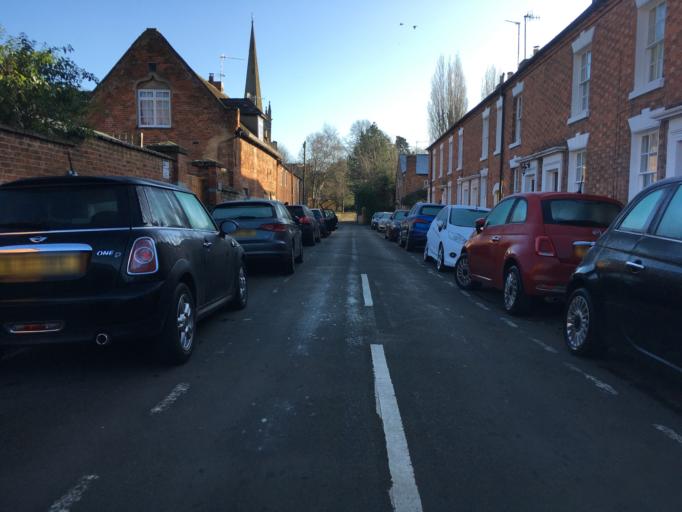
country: GB
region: England
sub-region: Warwickshire
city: Stratford-upon-Avon
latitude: 52.1868
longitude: -1.7094
